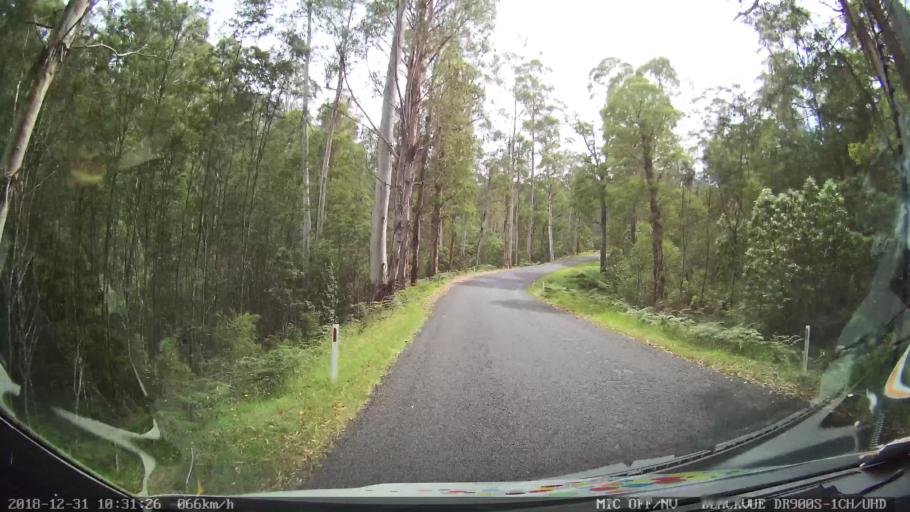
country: AU
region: New South Wales
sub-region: Snowy River
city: Jindabyne
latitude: -36.4575
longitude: 148.1580
